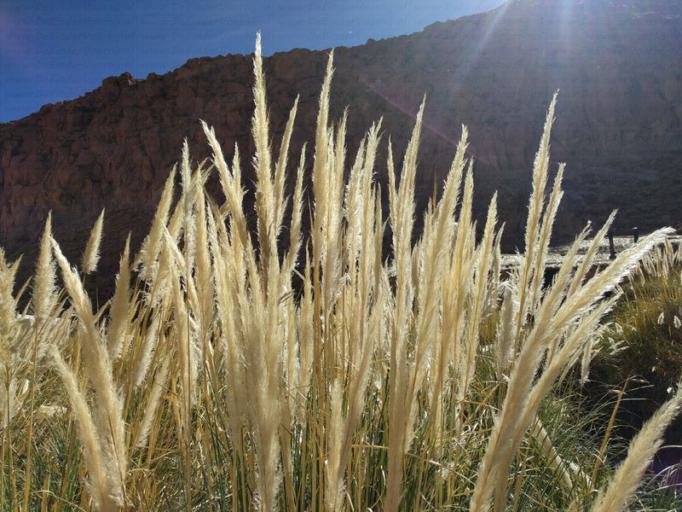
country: CL
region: Antofagasta
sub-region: Provincia de El Loa
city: San Pedro de Atacama
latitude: -22.7201
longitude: -68.0435
